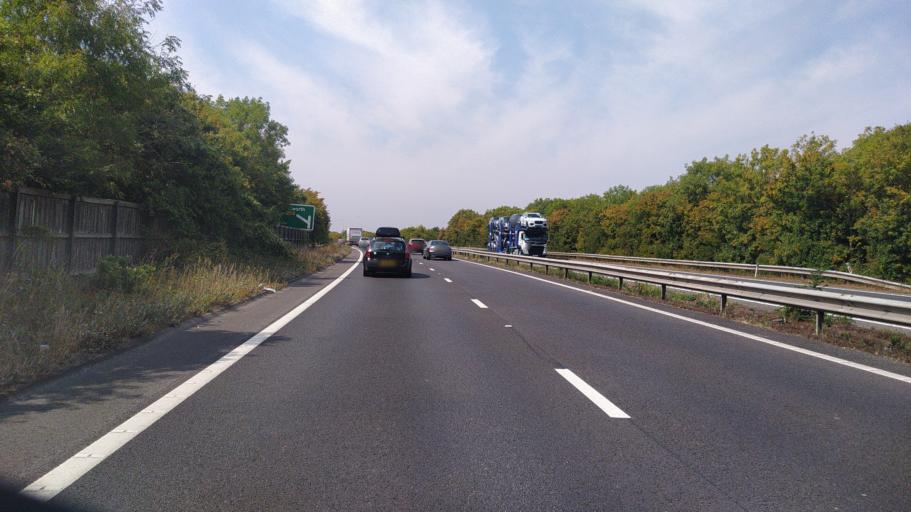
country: GB
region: England
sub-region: Hampshire
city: Emsworth
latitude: 50.8522
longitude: -0.9555
